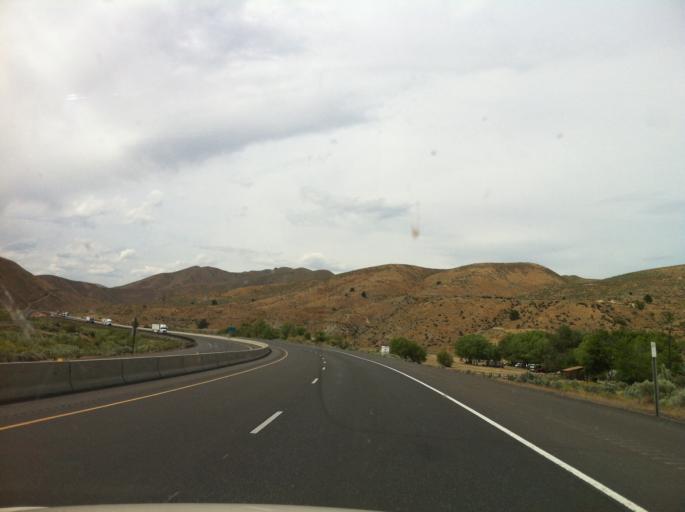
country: US
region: Idaho
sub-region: Washington County
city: Weiser
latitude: 44.4210
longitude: -117.3103
